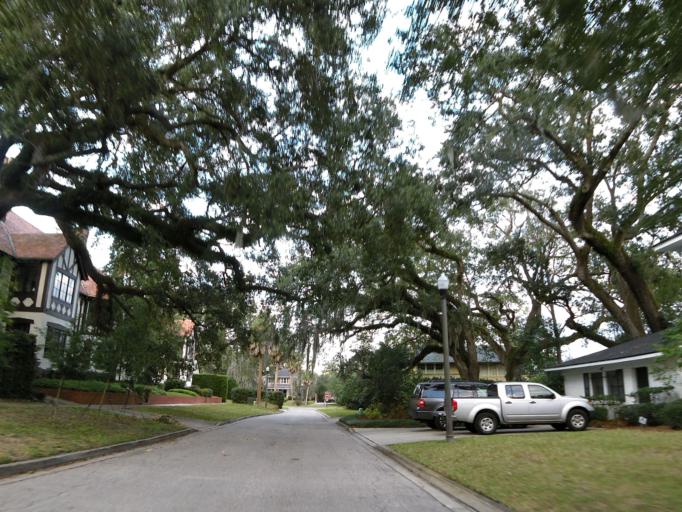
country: US
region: Florida
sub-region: Duval County
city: Jacksonville
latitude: 30.2984
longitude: -81.7004
